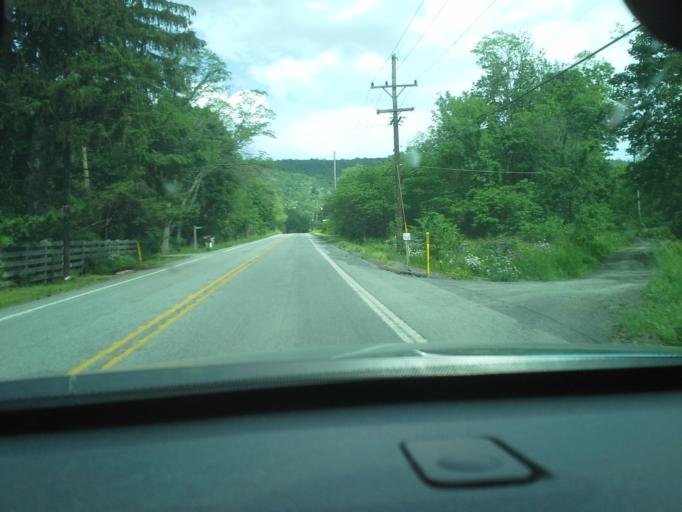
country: US
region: Pennsylvania
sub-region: Fulton County
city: McConnellsburg
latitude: 39.9186
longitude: -77.9753
